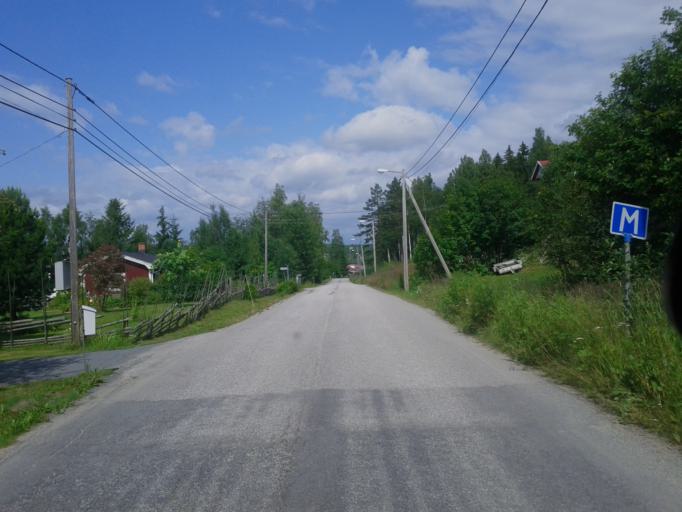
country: SE
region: Vaesternorrland
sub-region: OErnskoeldsviks Kommun
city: Ornskoldsvik
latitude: 63.2603
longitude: 18.8081
